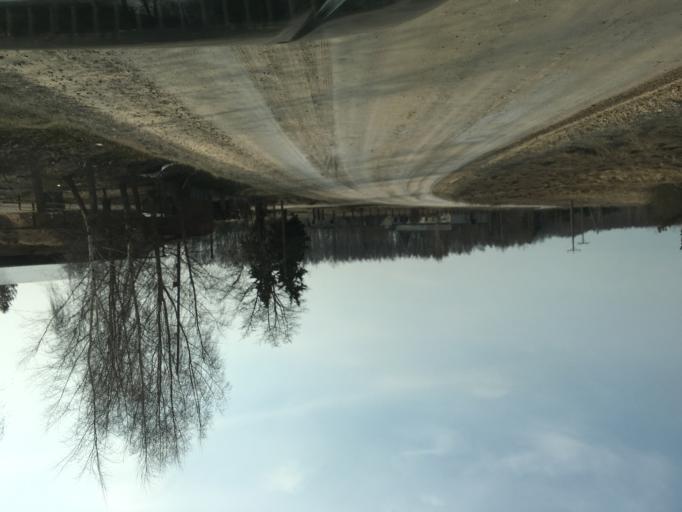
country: LV
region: Olaine
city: Olaine
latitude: 56.7949
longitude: 23.9821
